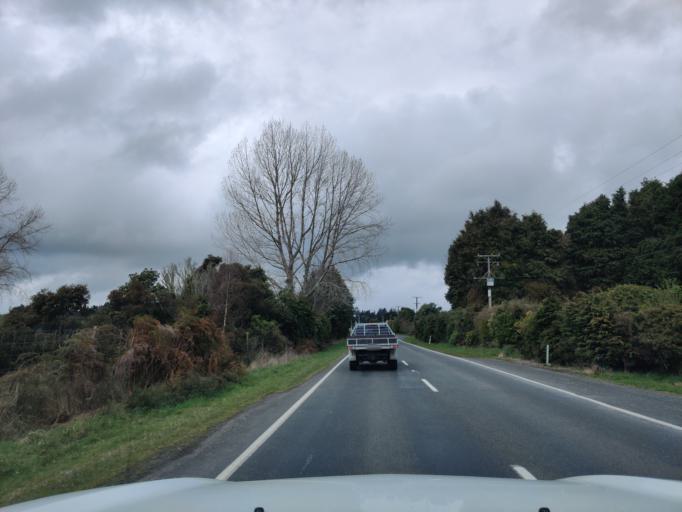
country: NZ
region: Manawatu-Wanganui
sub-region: Ruapehu District
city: Waiouru
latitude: -39.3676
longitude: 175.3189
